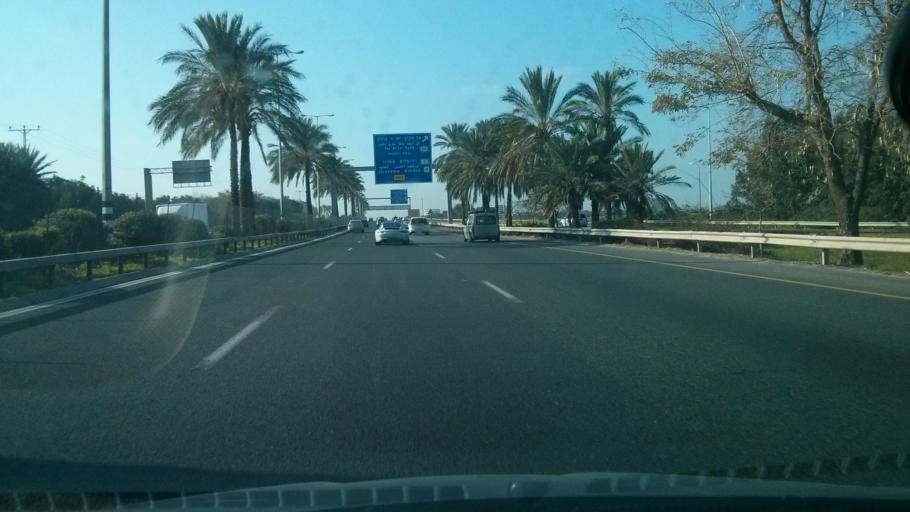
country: IL
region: Tel Aviv
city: Herzliya Pituah
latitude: 32.1548
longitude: 34.8075
